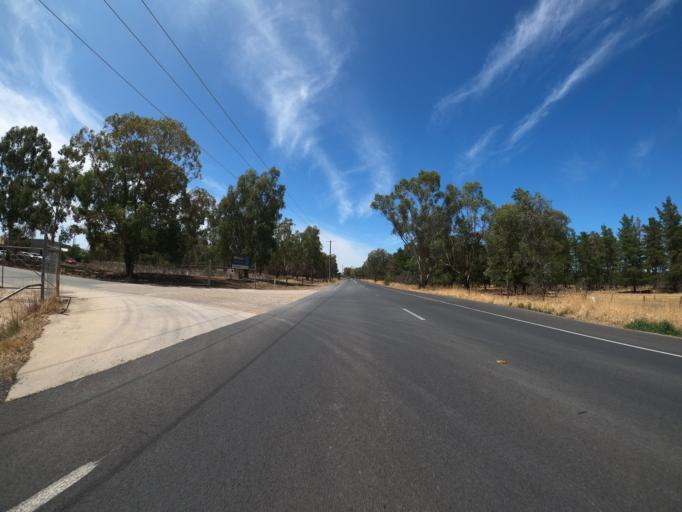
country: AU
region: Victoria
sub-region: Benalla
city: Benalla
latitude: -36.5266
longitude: 146.0389
